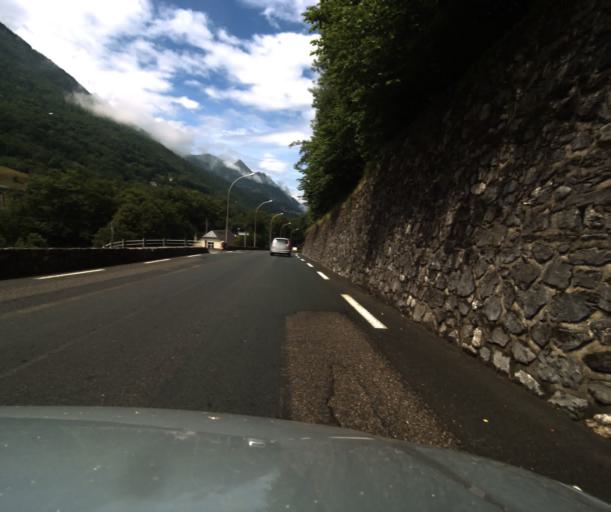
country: FR
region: Midi-Pyrenees
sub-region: Departement des Hautes-Pyrenees
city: Luz-Saint-Sauveur
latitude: 42.8635
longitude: -0.0076
